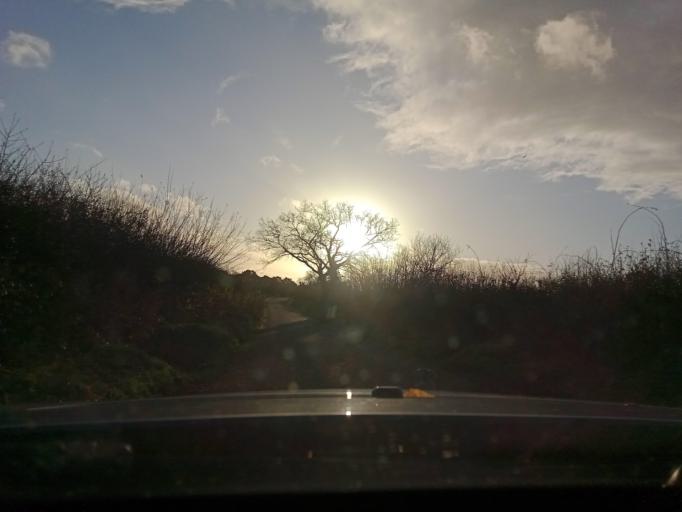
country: IE
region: Leinster
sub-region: Kilkenny
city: Callan
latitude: 52.5315
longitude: -7.3792
